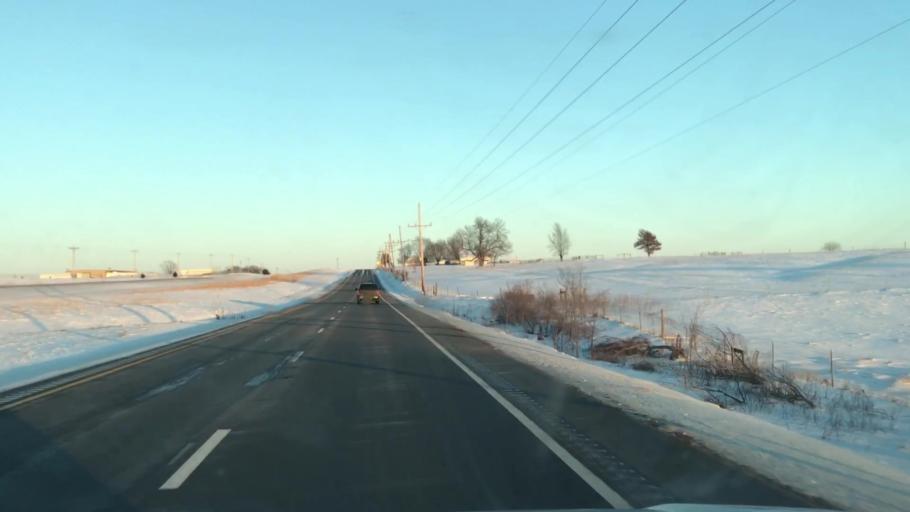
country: US
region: Missouri
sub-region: Clinton County
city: Cameron
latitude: 39.7546
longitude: -94.3077
